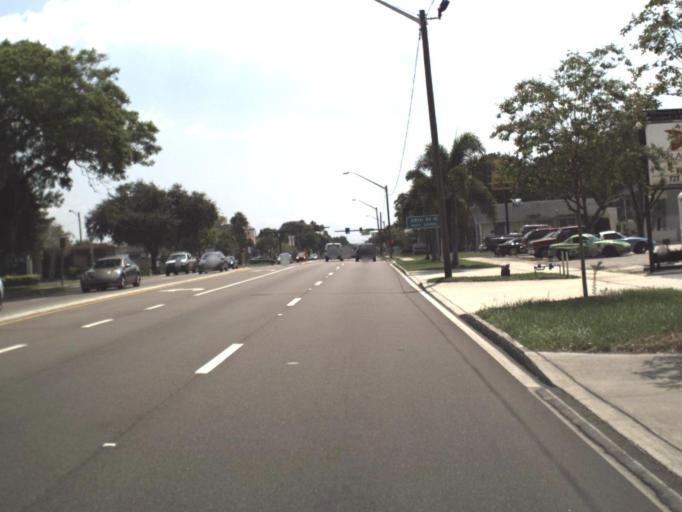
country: US
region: Florida
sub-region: Pinellas County
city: Saint Petersburg
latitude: 27.7773
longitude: -82.6735
